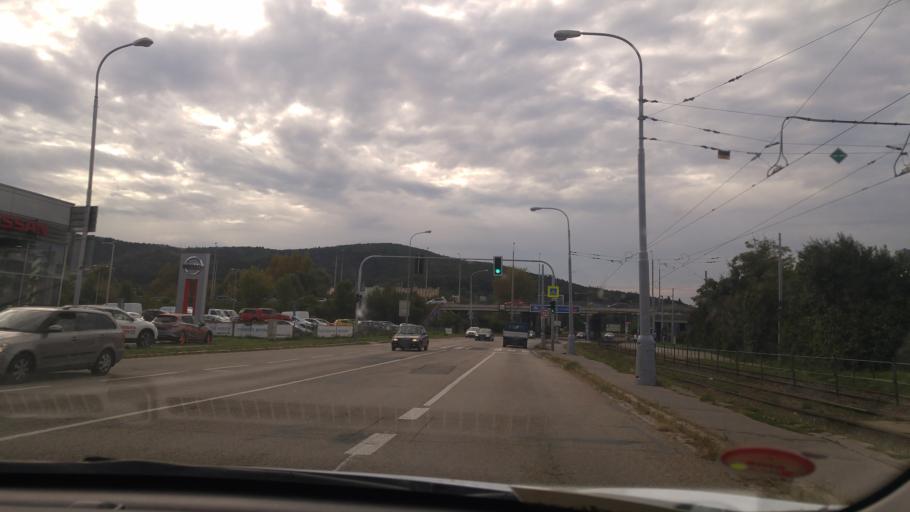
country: CZ
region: South Moravian
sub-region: Mesto Brno
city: Brno
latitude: 49.2128
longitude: 16.5613
